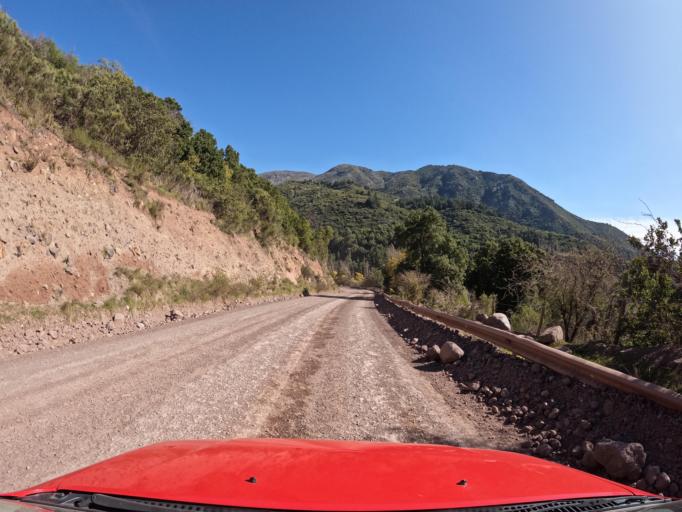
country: CL
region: O'Higgins
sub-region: Provincia de Colchagua
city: Chimbarongo
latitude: -35.0111
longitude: -70.7453
